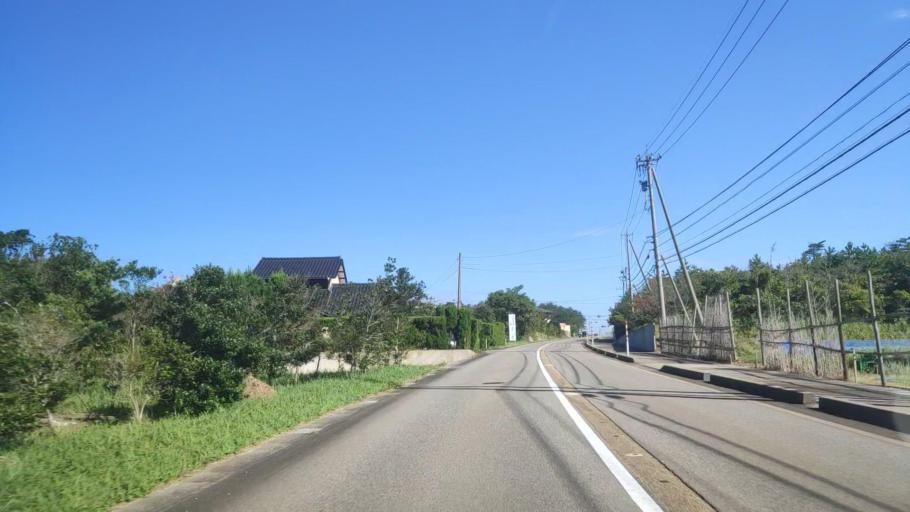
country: JP
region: Ishikawa
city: Hakui
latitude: 36.9856
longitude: 136.7757
